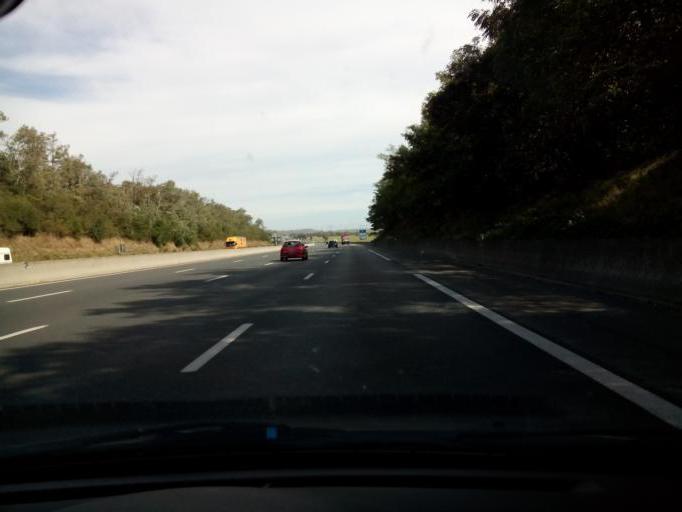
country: FR
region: Rhone-Alpes
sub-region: Departement du Rhone
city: Saint-Bonnet-de-Mure
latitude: 45.6867
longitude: 4.9977
